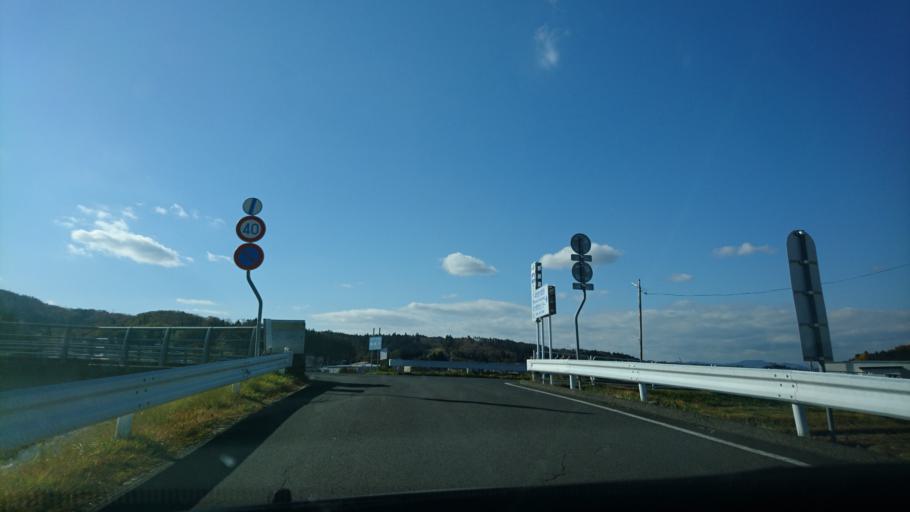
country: JP
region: Iwate
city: Ichinoseki
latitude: 39.0151
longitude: 141.3945
